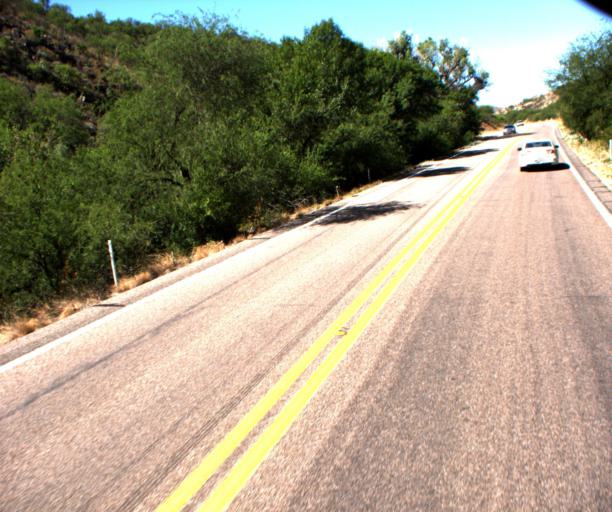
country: US
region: Arizona
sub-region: Santa Cruz County
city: Rio Rico
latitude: 31.5067
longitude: -110.8045
